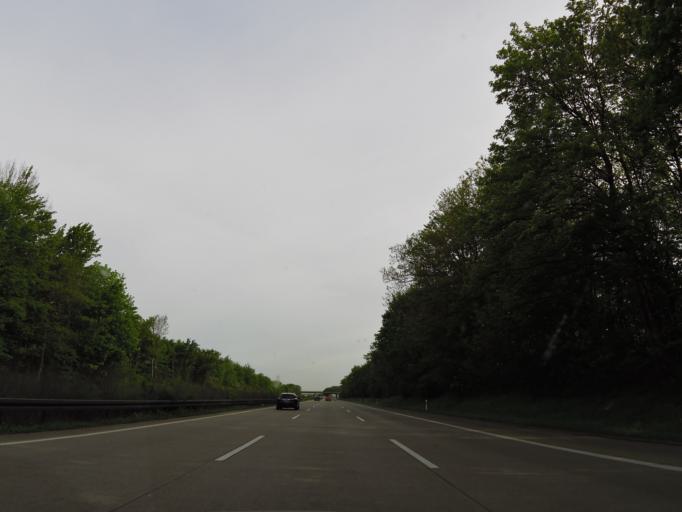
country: DE
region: Lower Saxony
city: Harsum
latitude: 52.2189
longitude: 9.9339
